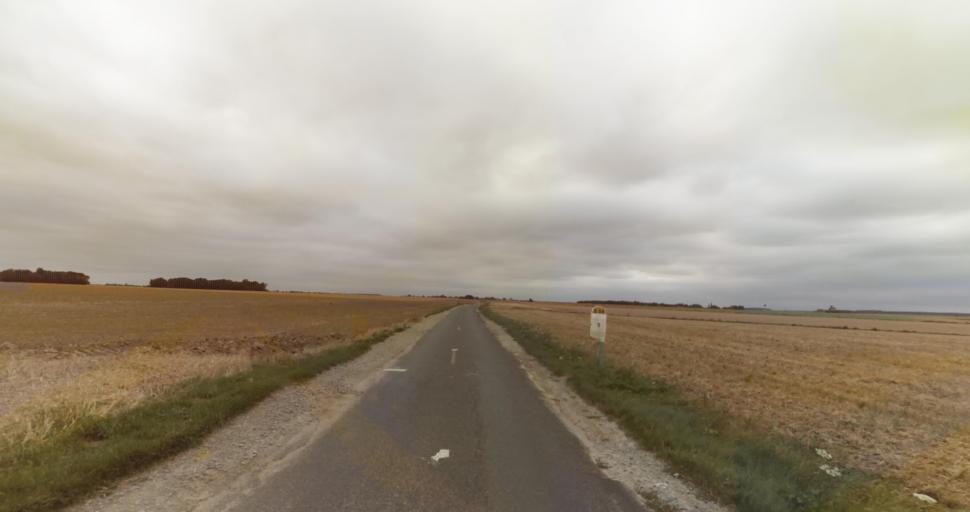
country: FR
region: Haute-Normandie
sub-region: Departement de l'Eure
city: La Couture-Boussey
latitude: 48.9138
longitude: 1.3410
